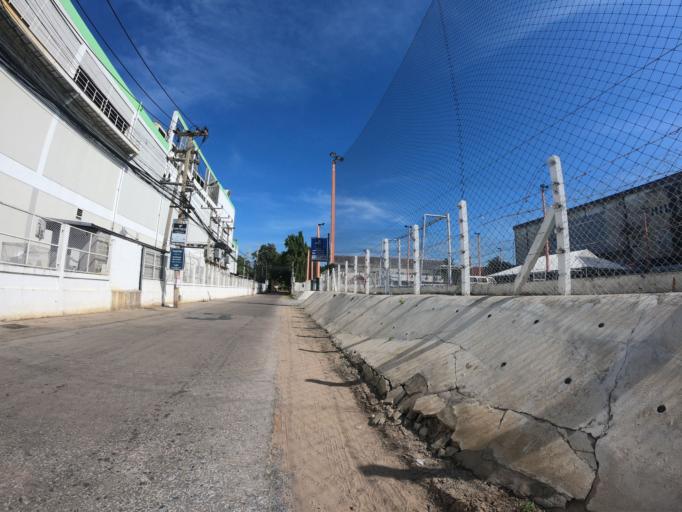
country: TH
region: Nakhon Ratchasima
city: Nakhon Ratchasima
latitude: 14.9813
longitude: 102.0929
